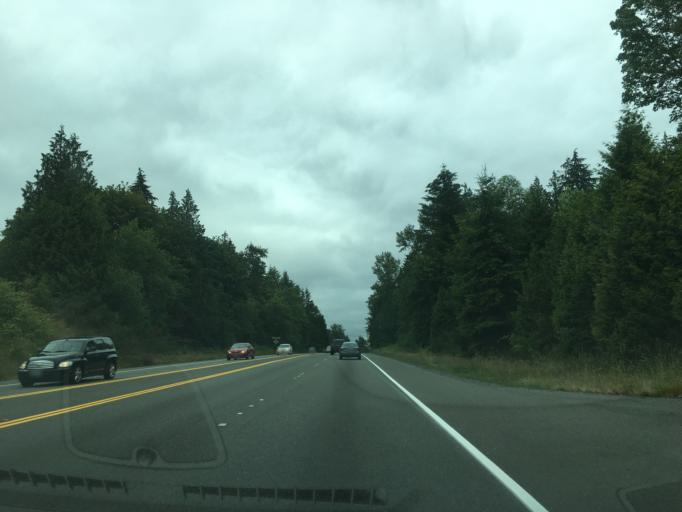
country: US
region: Washington
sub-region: Snohomish County
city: West Lake Stevens
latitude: 47.9952
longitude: -122.1212
